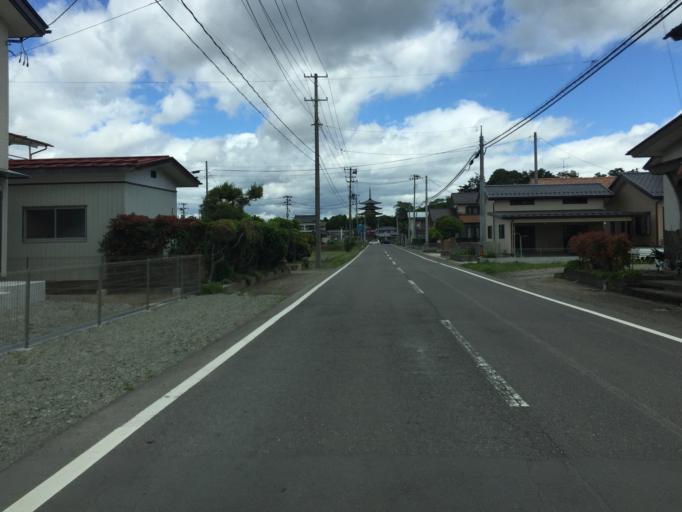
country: JP
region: Fukushima
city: Nihommatsu
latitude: 37.5917
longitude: 140.4620
